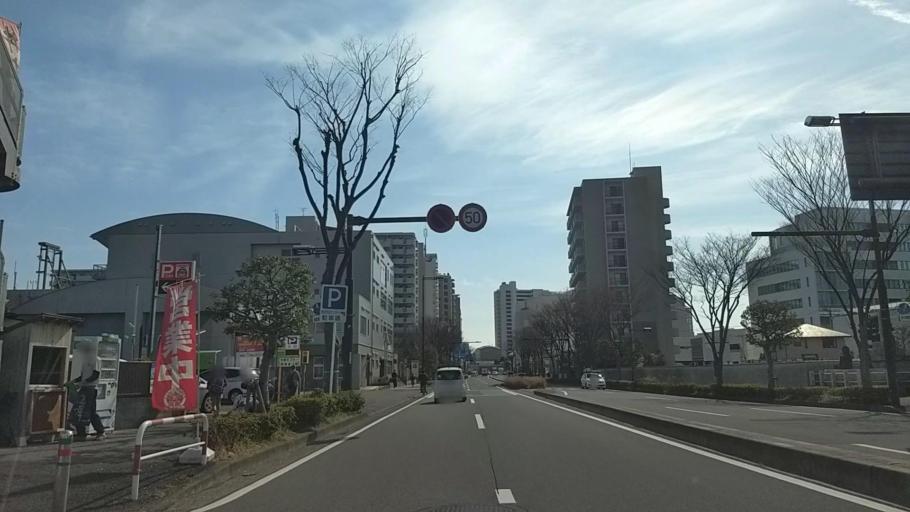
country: JP
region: Kanagawa
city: Fujisawa
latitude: 35.3411
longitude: 139.4492
